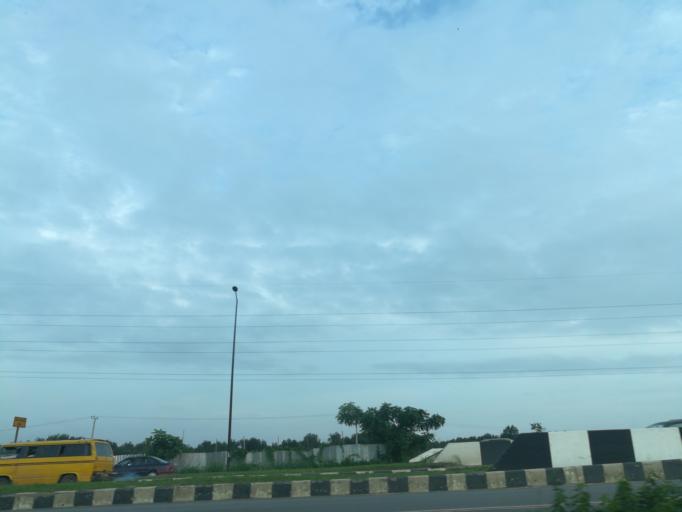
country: NG
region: Lagos
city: Ebute Ikorodu
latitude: 6.6173
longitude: 3.4472
